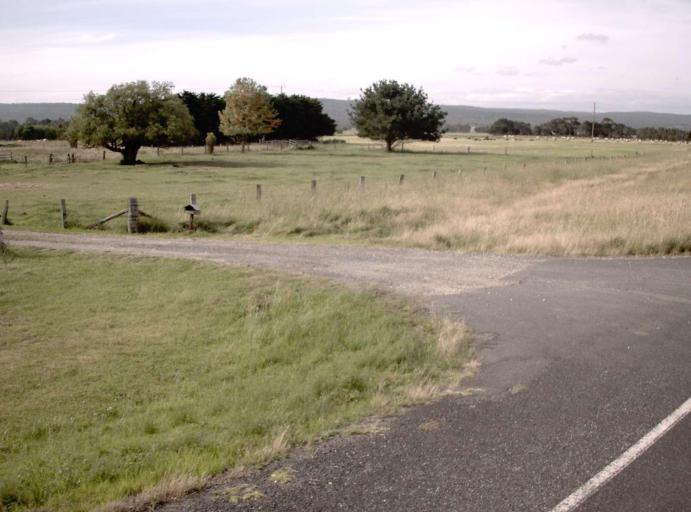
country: AU
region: Victoria
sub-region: Latrobe
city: Traralgon
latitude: -38.1056
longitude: 146.5927
